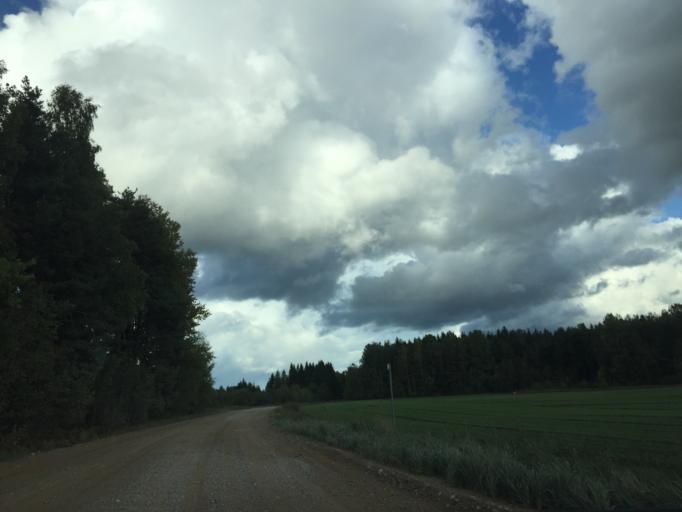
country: LV
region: Malpils
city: Malpils
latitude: 57.0527
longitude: 25.1226
